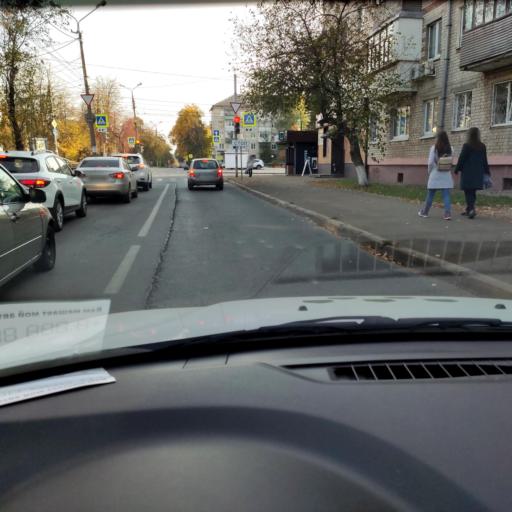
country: RU
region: Samara
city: Tol'yatti
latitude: 53.5083
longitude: 49.4116
